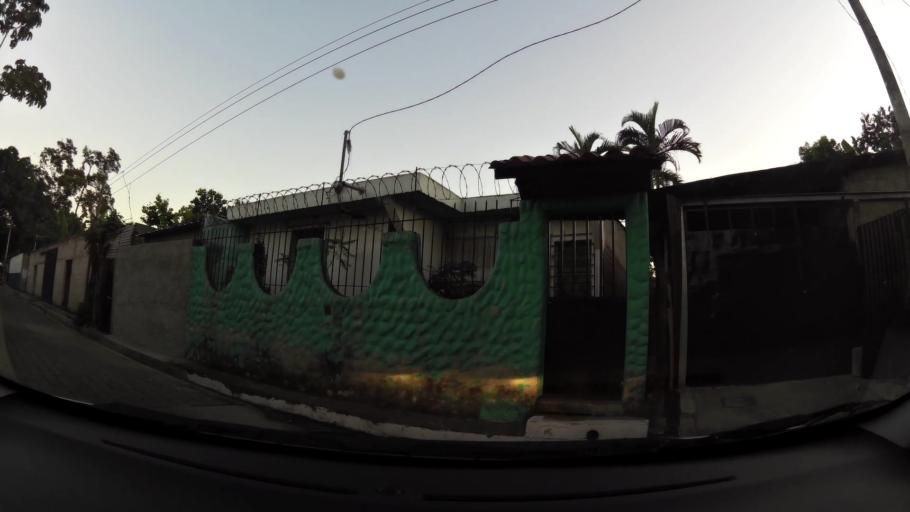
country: SV
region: La Libertad
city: Santa Tecla
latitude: 13.7321
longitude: -89.3790
